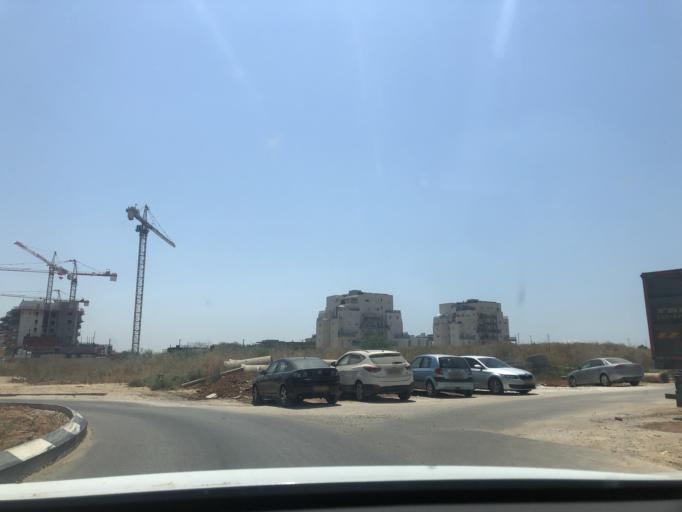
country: IL
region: Central District
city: Lod
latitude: 31.9382
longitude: 34.8983
